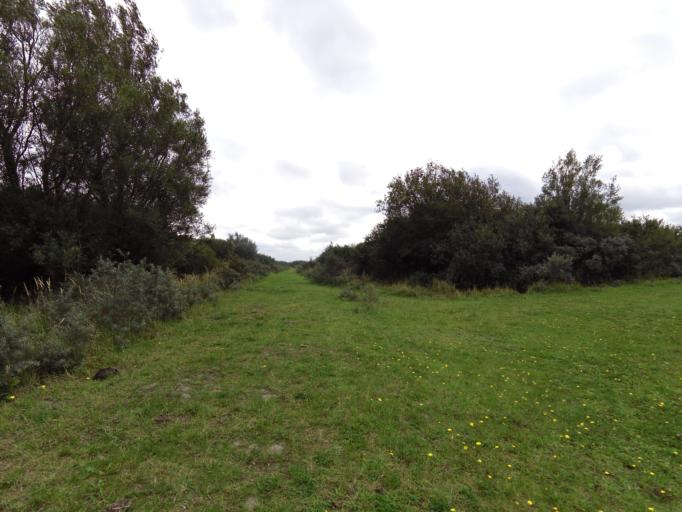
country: NL
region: South Holland
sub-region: Gemeente Goeree-Overflakkee
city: Dirksland
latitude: 51.7615
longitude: 4.0321
